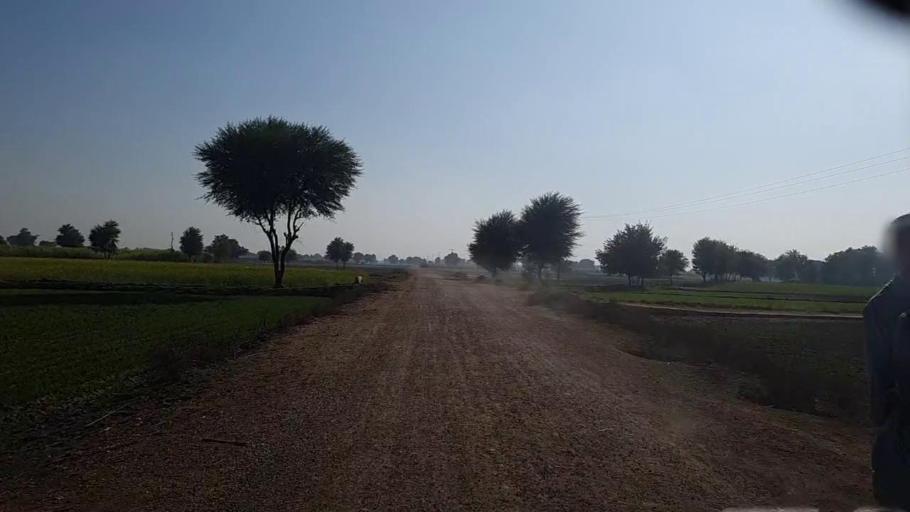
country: PK
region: Sindh
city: Darya Khan Marri
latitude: 26.6634
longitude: 68.3363
